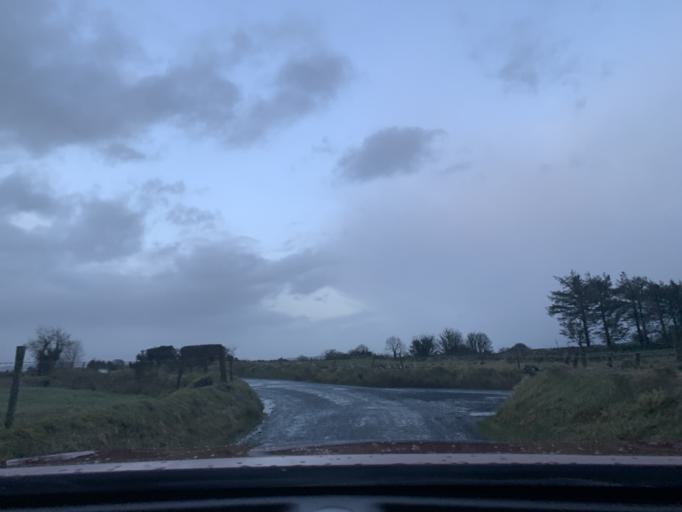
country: IE
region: Connaught
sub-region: Roscommon
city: Ballaghaderreen
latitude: 53.9798
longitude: -8.5463
